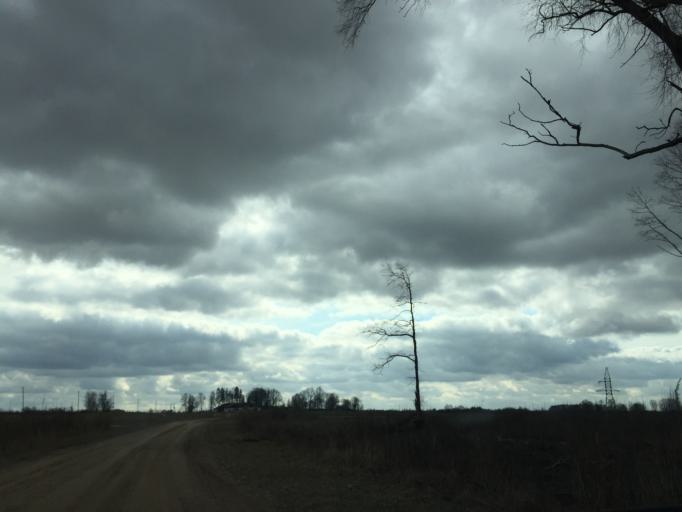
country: LV
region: Vecumnieki
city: Vecumnieki
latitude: 56.5652
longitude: 24.6006
